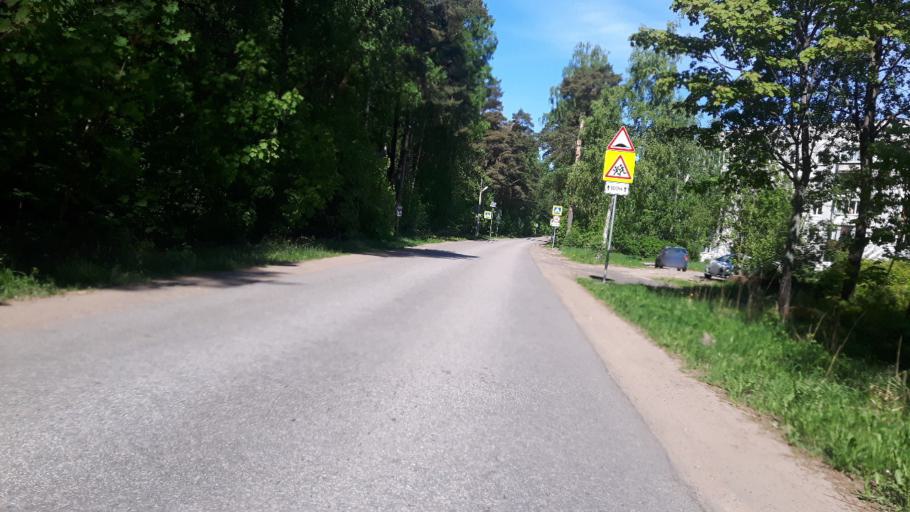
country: RU
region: Leningrad
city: Lebyazh'ye
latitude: 59.9621
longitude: 29.4131
